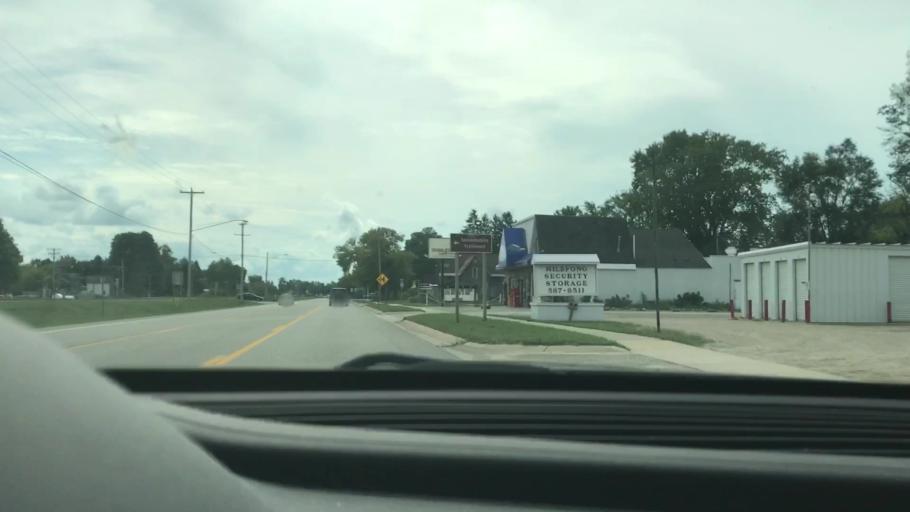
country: US
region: Michigan
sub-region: Antrim County
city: Mancelona
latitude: 44.8965
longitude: -85.0670
